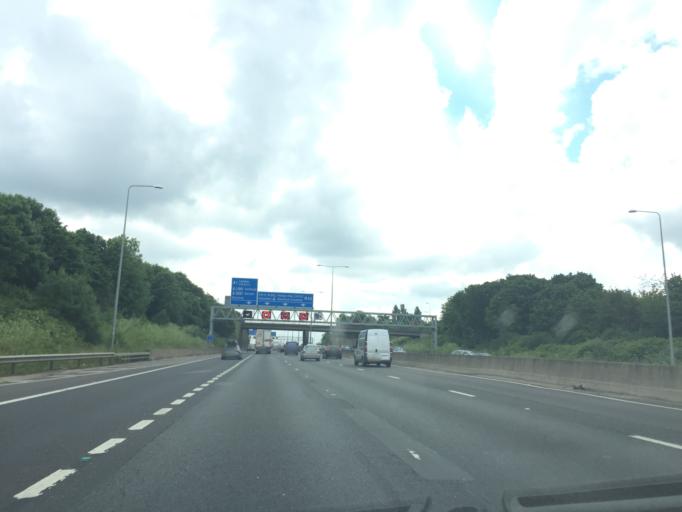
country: GB
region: England
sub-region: Hertfordshire
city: Shenley AV
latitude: 51.6929
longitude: -0.2376
